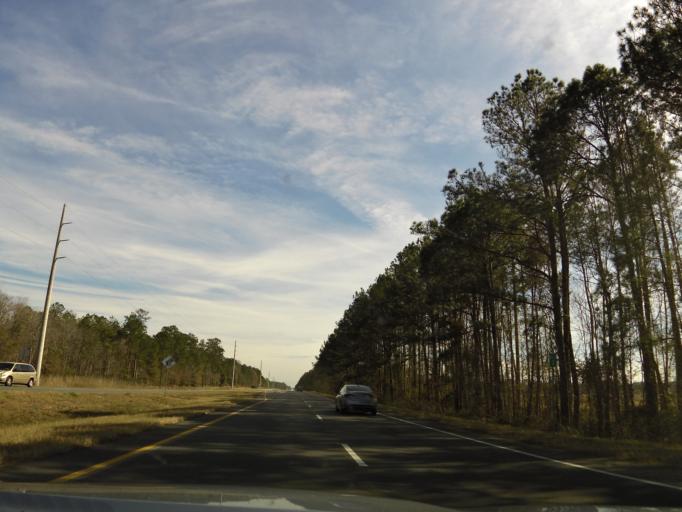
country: US
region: Georgia
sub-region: Glynn County
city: Dock Junction
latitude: 31.2157
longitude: -81.7166
